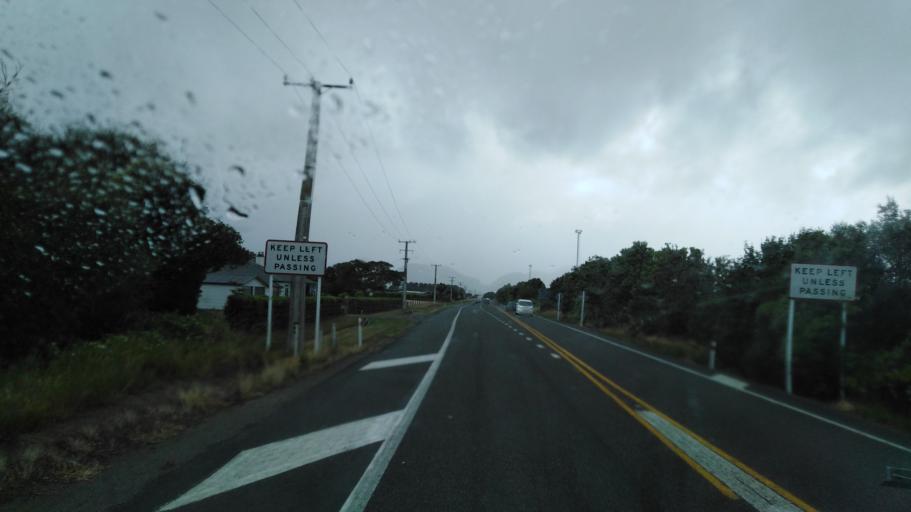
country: NZ
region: Marlborough
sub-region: Marlborough District
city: Blenheim
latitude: -41.4579
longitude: 173.9626
